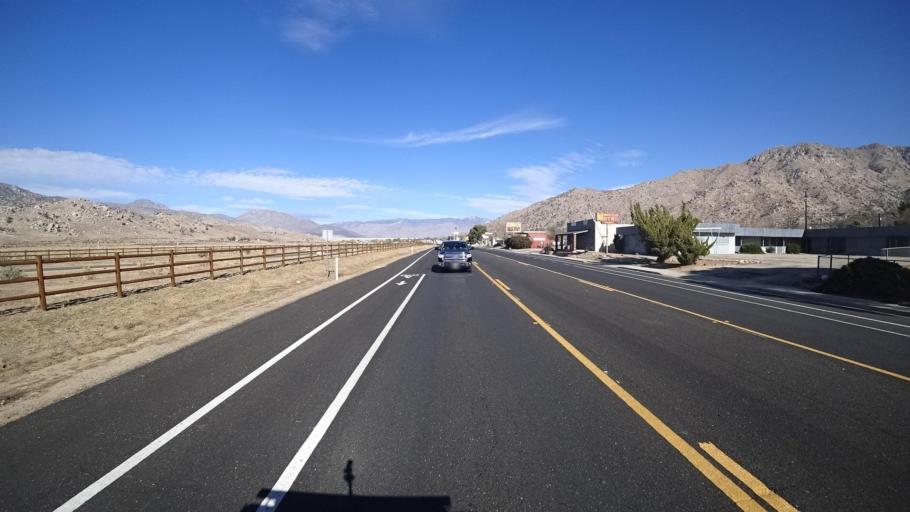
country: US
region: California
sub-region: Kern County
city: Lake Isabella
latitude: 35.6150
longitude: -118.4786
